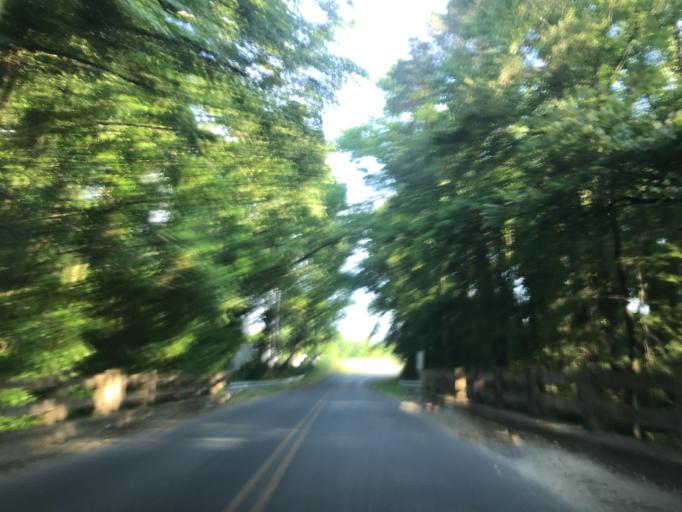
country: US
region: Maryland
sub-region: Caroline County
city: Federalsburg
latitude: 38.7111
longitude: -75.7767
